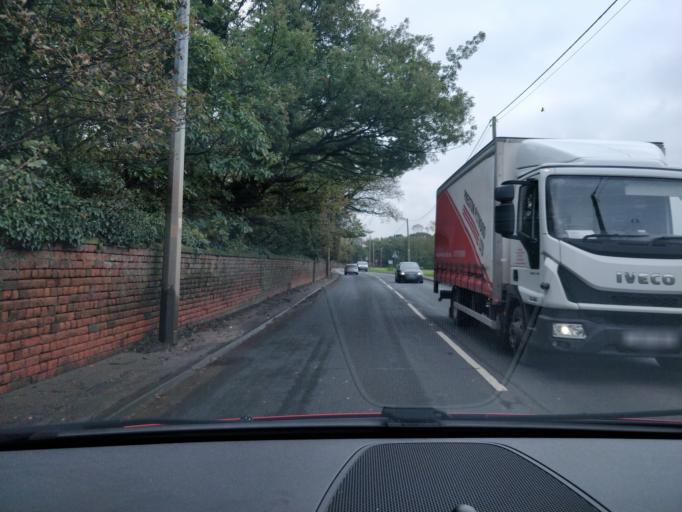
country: GB
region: England
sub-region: Lancashire
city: Ormskirk
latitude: 53.6092
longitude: -2.9338
